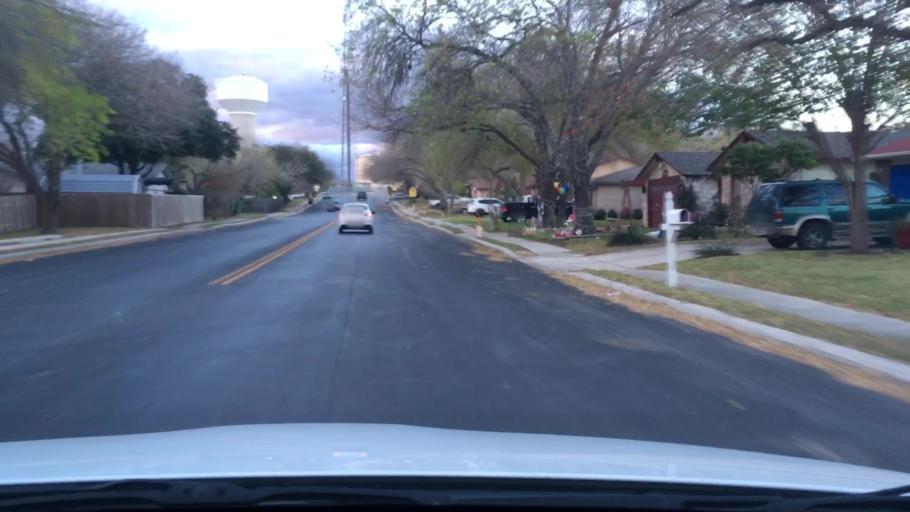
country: US
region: Texas
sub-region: Bexar County
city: Windcrest
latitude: 29.5268
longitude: -98.3531
